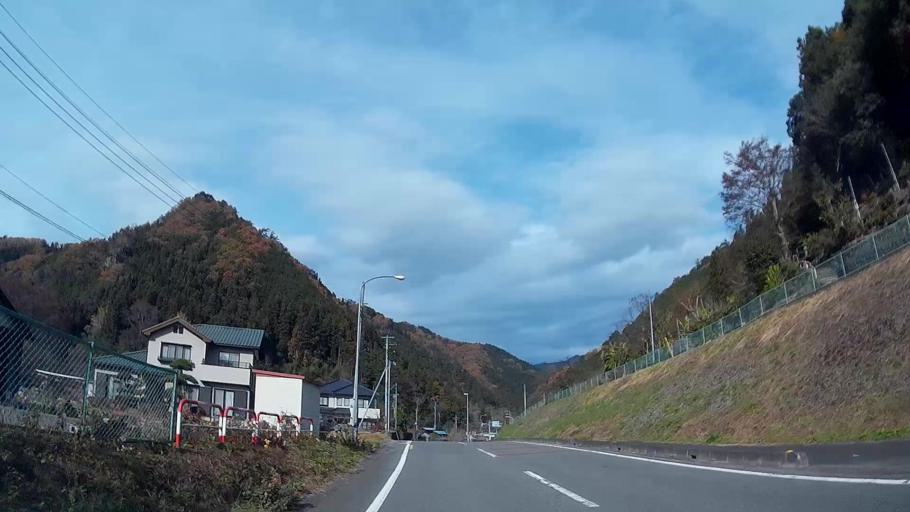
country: JP
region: Saitama
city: Chichibu
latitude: 36.0609
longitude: 138.9704
